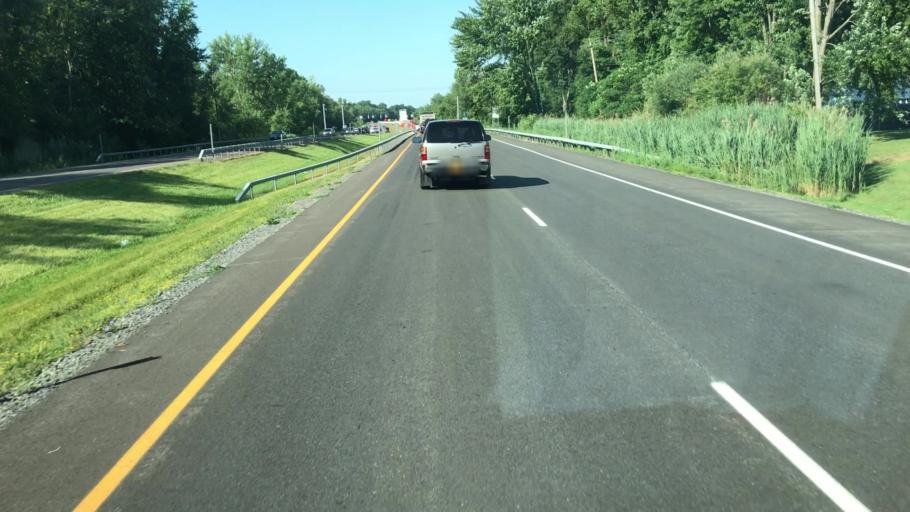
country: US
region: New York
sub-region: Onondaga County
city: Liverpool
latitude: 43.1270
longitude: -76.2434
